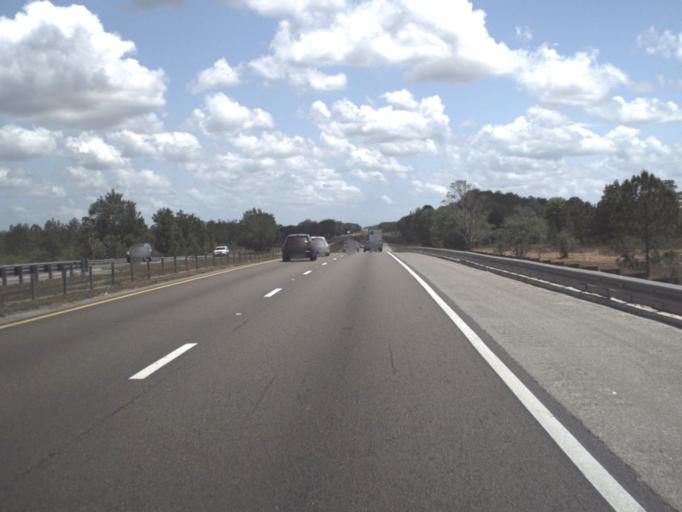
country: US
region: Florida
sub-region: Orange County
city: Wedgefield
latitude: 28.4515
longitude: -81.1412
